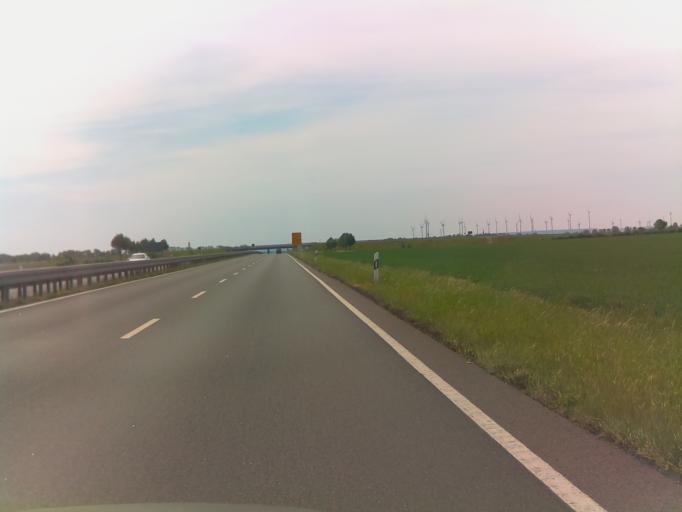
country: DE
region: Saxony-Anhalt
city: Wolmirsleben
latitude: 52.0203
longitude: 11.5115
